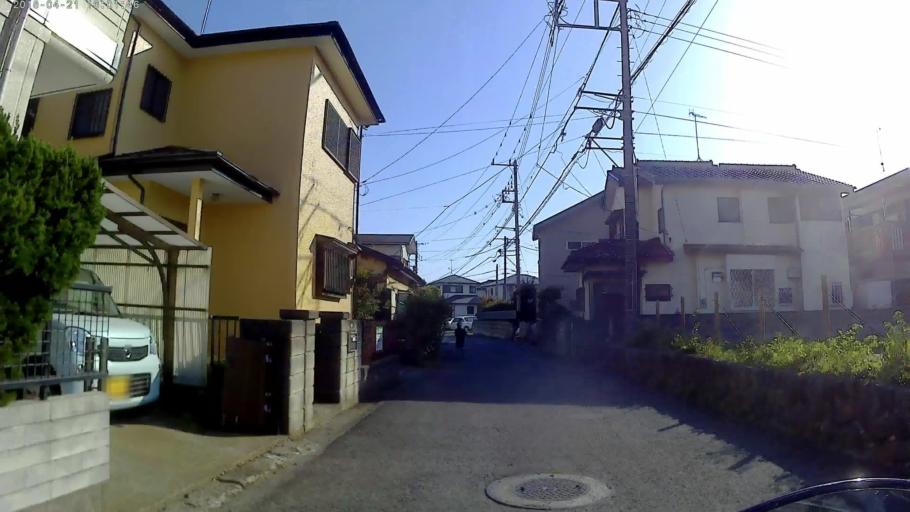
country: JP
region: Kanagawa
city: Fujisawa
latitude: 35.3391
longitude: 139.4388
